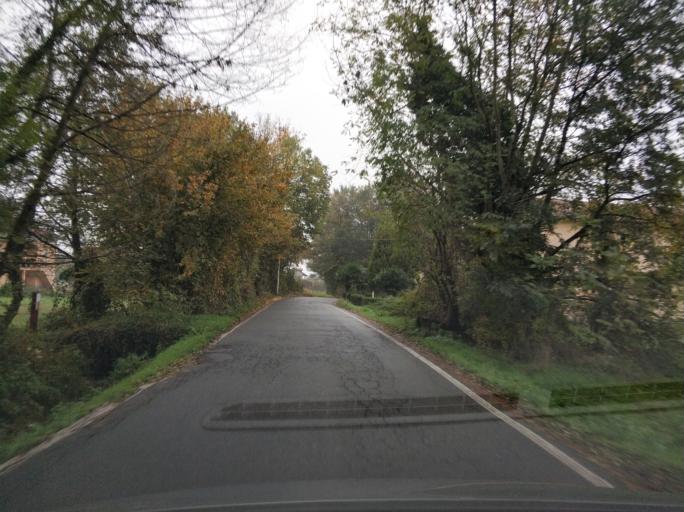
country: IT
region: Piedmont
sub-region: Provincia di Torino
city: Nole
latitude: 45.2314
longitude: 7.5780
